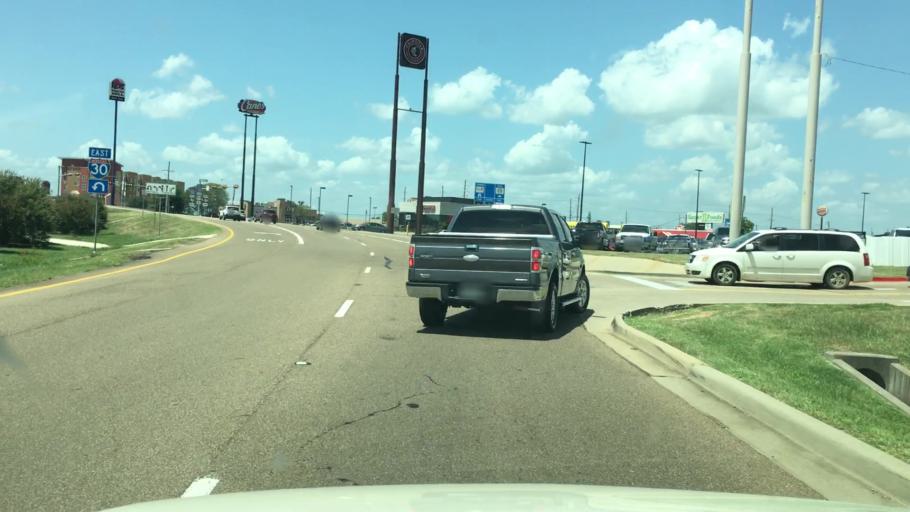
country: US
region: Texas
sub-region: Bowie County
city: Wake Village
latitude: 33.4578
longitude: -94.0861
